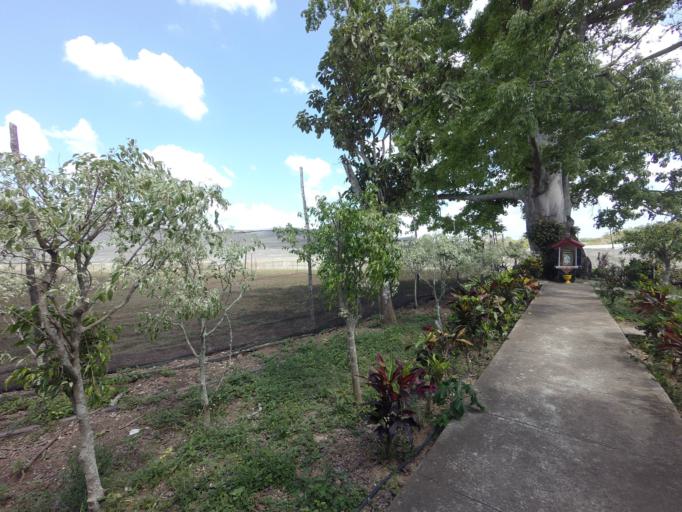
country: CU
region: Pinar del Rio
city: San Luis
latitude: 22.3120
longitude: -83.7623
